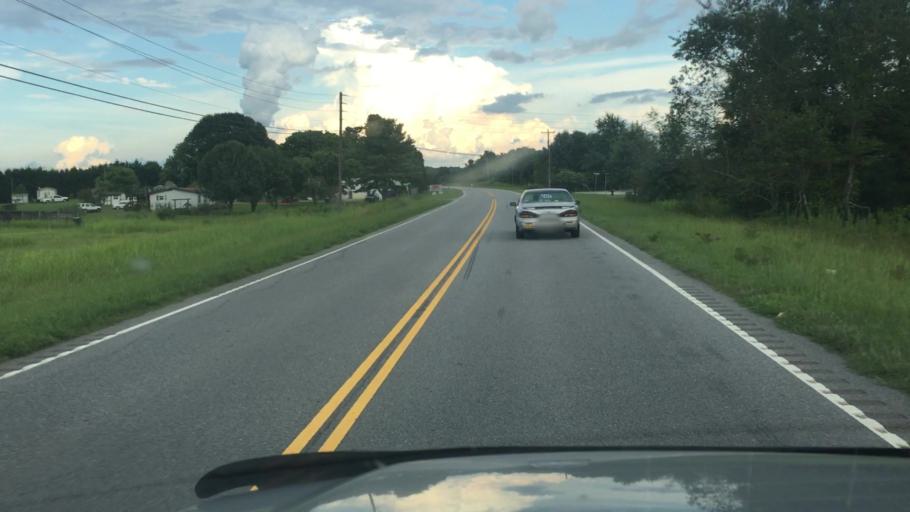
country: US
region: South Carolina
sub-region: Spartanburg County
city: Mayo
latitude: 35.1320
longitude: -81.7983
